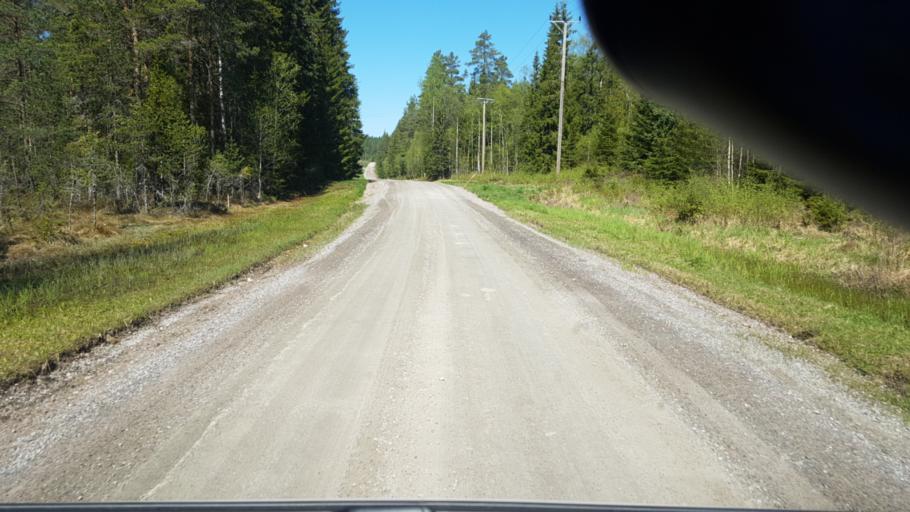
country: SE
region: Vaermland
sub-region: Arvika Kommun
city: Arvika
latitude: 59.8607
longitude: 12.7148
